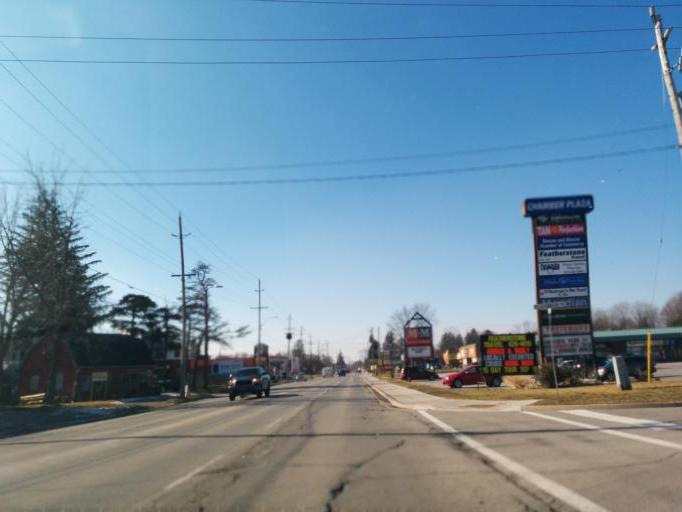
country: CA
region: Ontario
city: Norfolk County
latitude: 42.8457
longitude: -80.3101
